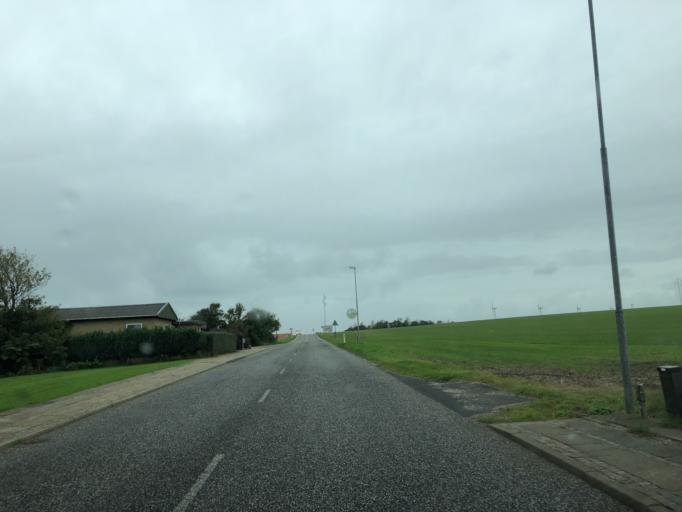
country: DK
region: North Denmark
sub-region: Thisted Kommune
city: Hurup
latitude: 56.7145
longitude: 8.3961
